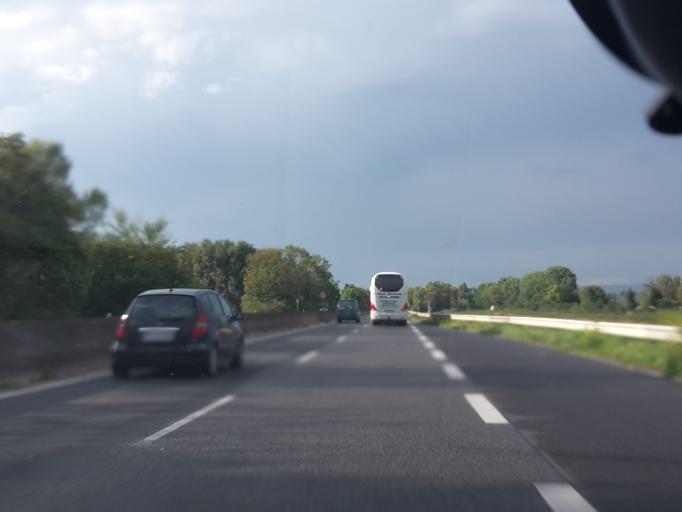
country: DE
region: Hesse
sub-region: Regierungsbezirk Darmstadt
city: Ginsheim-Gustavsburg
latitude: 49.9580
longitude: 8.3316
